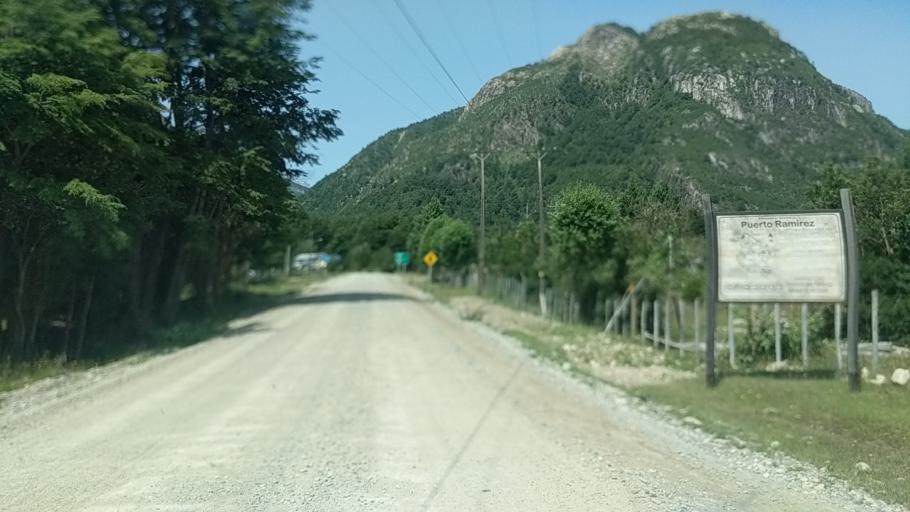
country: CL
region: Los Lagos
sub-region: Provincia de Palena
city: Palena
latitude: -43.4668
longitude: -72.1213
